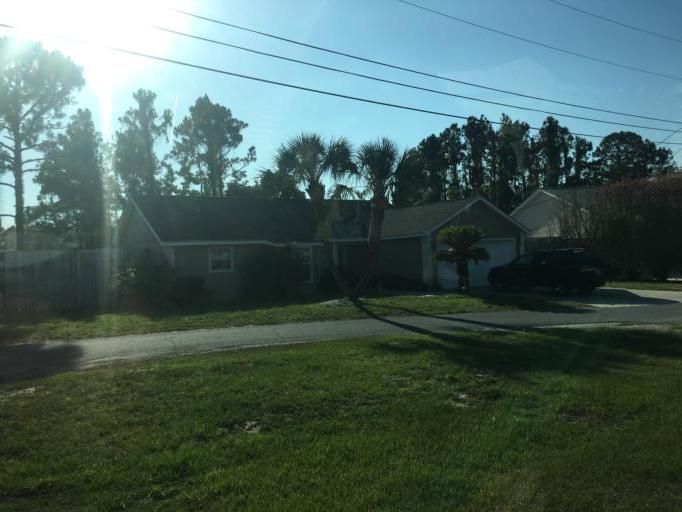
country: US
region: Florida
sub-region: Bay County
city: Panama City Beach
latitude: 30.2086
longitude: -85.8280
